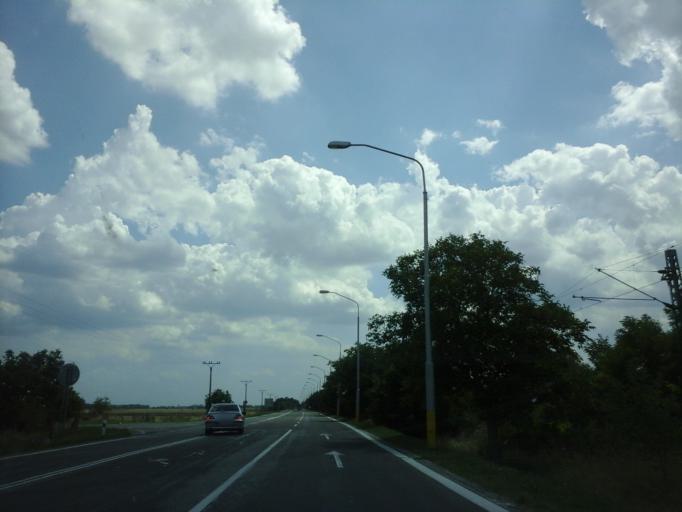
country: HU
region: Gyor-Moson-Sopron
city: Rajka
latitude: 48.0264
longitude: 17.1700
